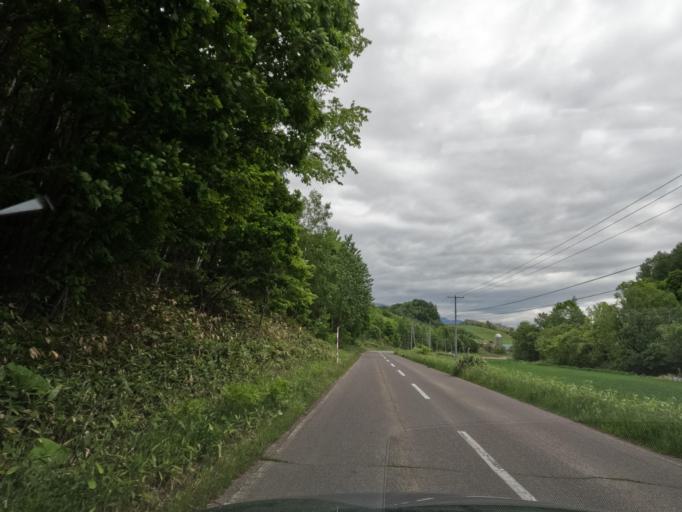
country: JP
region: Hokkaido
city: Shimo-furano
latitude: 43.4749
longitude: 142.4281
